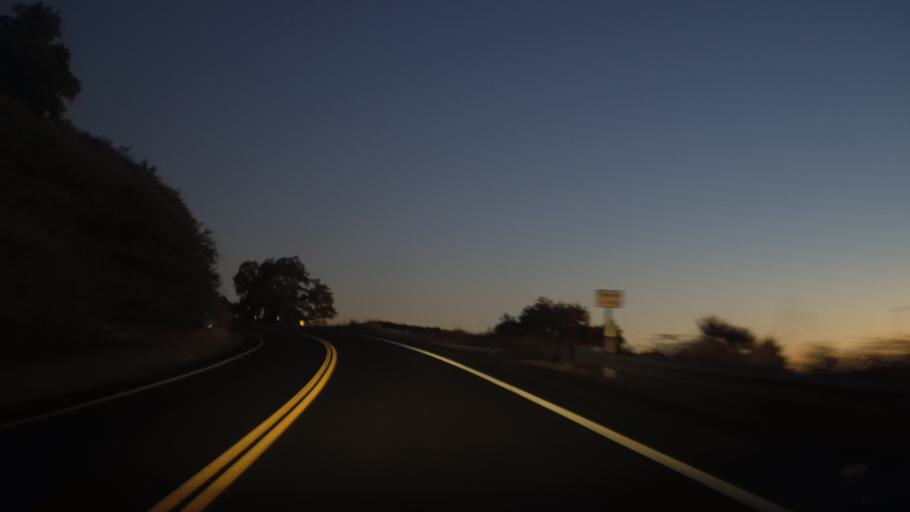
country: US
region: California
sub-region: San Diego County
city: Julian
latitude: 33.1046
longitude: -116.6684
